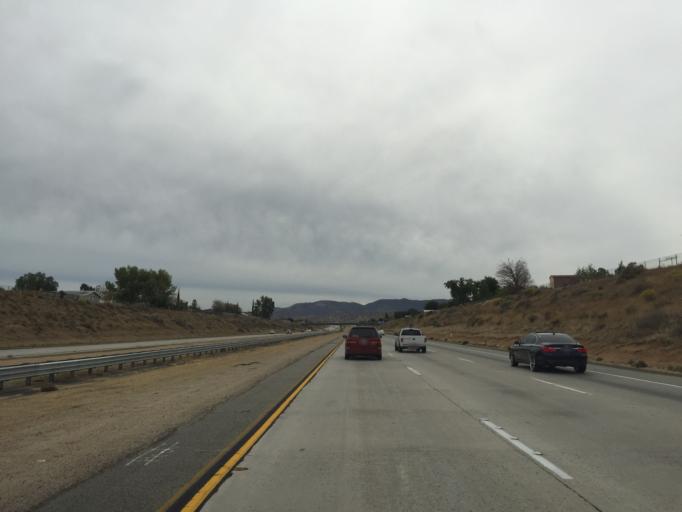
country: US
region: California
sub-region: Los Angeles County
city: Desert View Highlands
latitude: 34.6218
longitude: -118.1535
